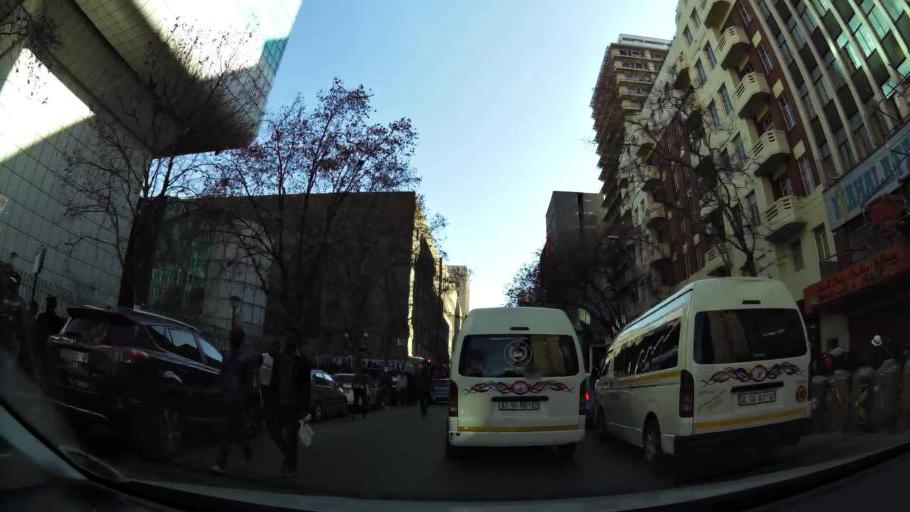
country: ZA
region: Gauteng
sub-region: City of Johannesburg Metropolitan Municipality
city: Johannesburg
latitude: -26.2010
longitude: 28.0466
